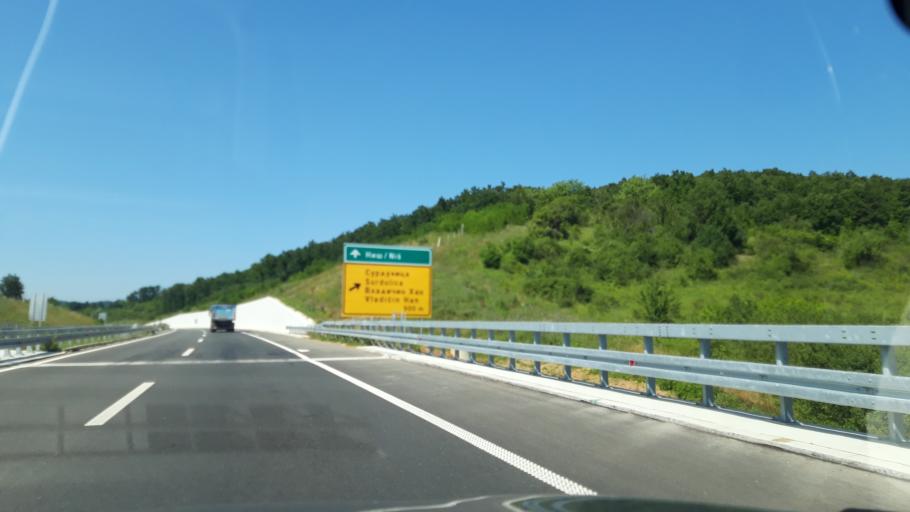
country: RS
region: Central Serbia
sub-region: Pcinjski Okrug
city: Vladicin Han
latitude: 42.6947
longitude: 22.0757
